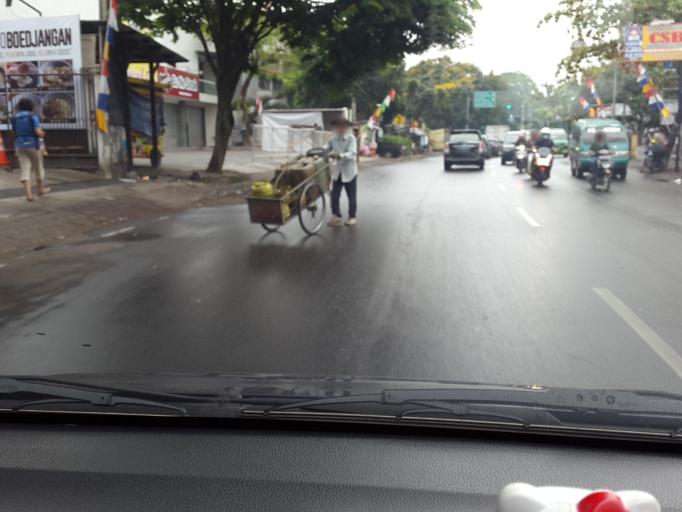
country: ID
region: West Java
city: Bandung
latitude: -6.8991
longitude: 107.6340
